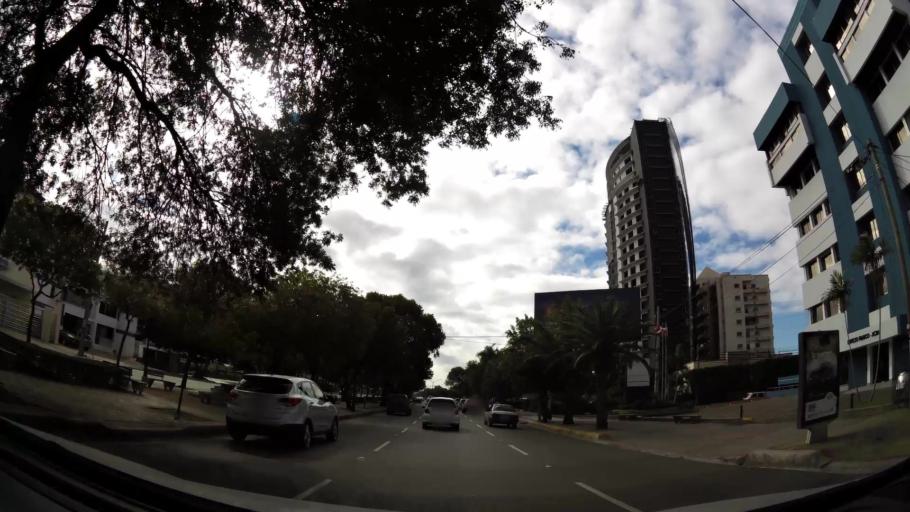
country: DO
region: Nacional
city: La Julia
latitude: 18.4598
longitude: -69.9335
